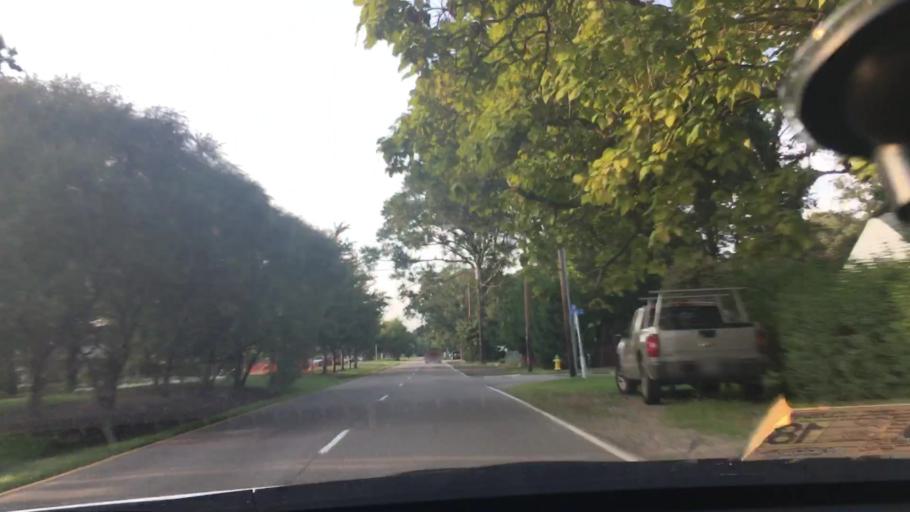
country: US
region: Virginia
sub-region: City of Norfolk
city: Norfolk
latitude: 36.9379
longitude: -76.2449
